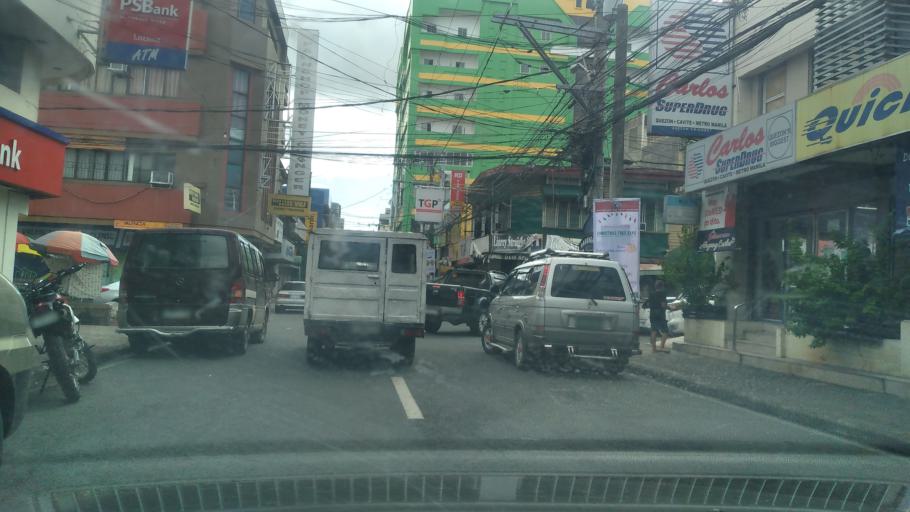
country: PH
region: Calabarzon
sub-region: Province of Quezon
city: Lucena
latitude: 13.9331
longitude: 121.6128
